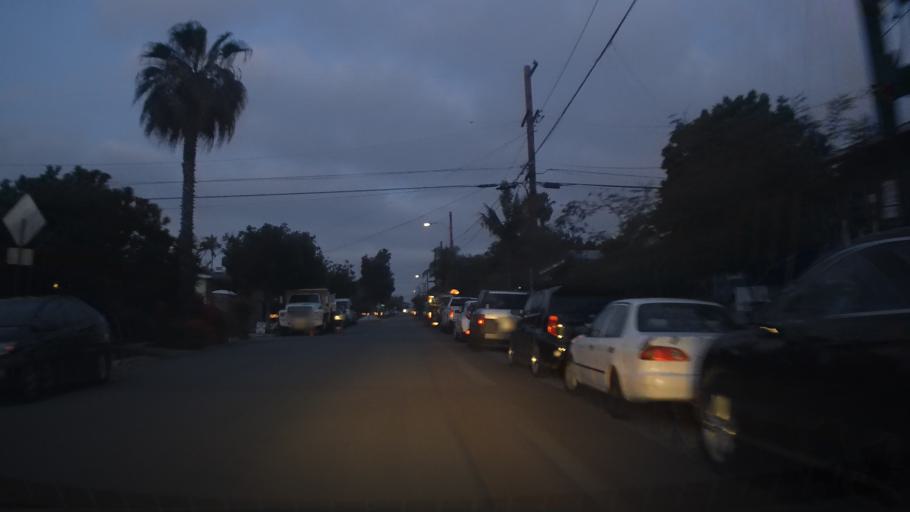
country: US
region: California
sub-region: San Diego County
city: San Diego
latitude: 32.7654
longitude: -117.1216
